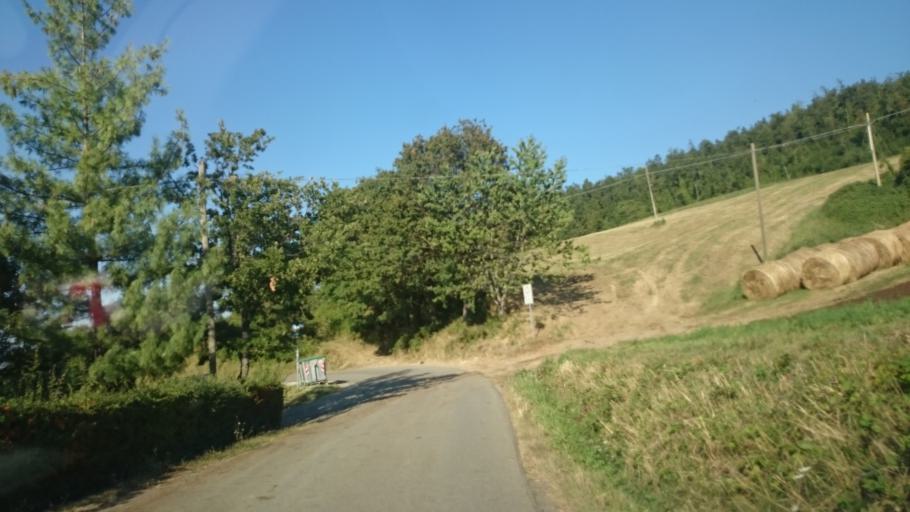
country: IT
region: Emilia-Romagna
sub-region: Provincia di Reggio Emilia
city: Villa Minozzo
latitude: 44.3436
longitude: 10.4817
